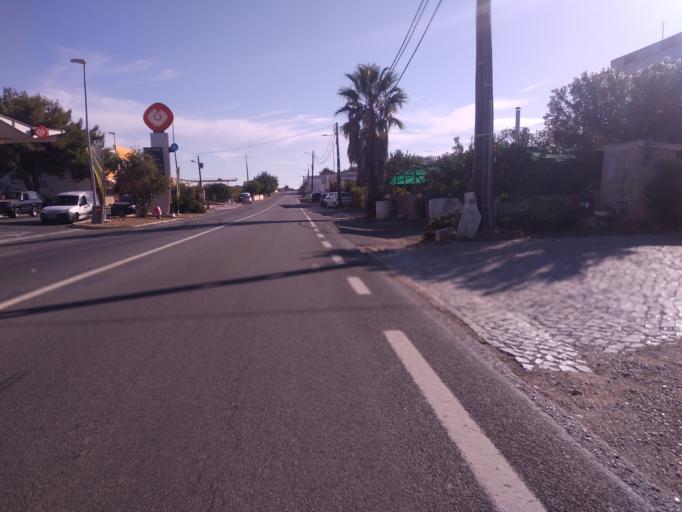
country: PT
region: Faro
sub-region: Sao Bras de Alportel
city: Sao Bras de Alportel
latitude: 37.0979
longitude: -7.9060
